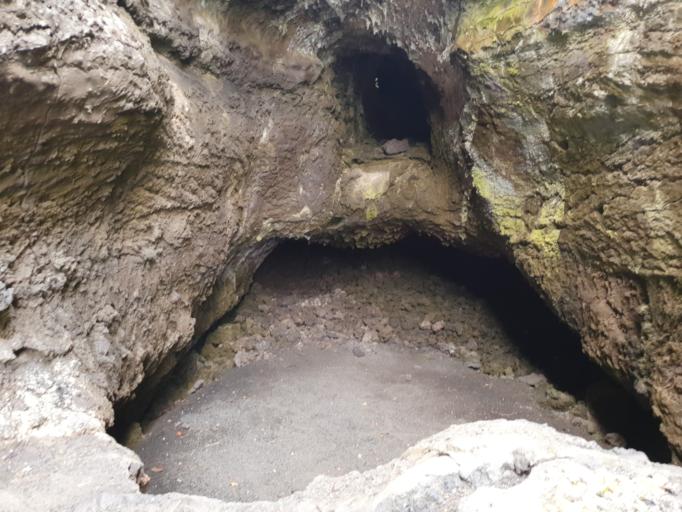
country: ES
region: Canary Islands
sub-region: Provincia de Las Palmas
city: Tinajo
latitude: 29.0117
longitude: -13.7184
